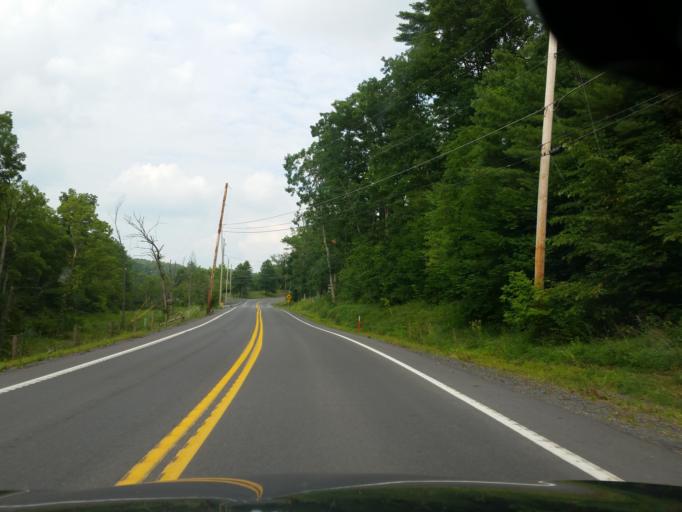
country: US
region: Pennsylvania
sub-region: Union County
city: New Columbia
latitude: 41.0181
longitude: -76.9244
